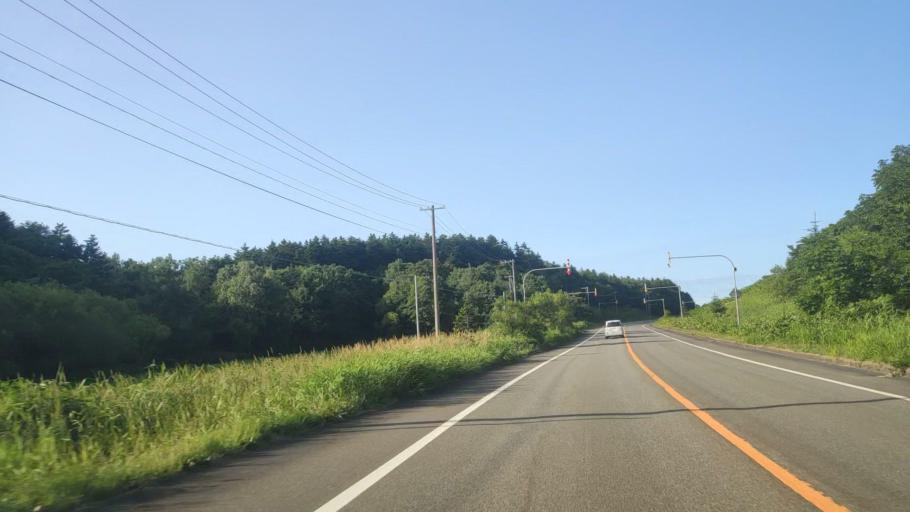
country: JP
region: Hokkaido
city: Makubetsu
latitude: 45.0800
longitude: 141.7536
